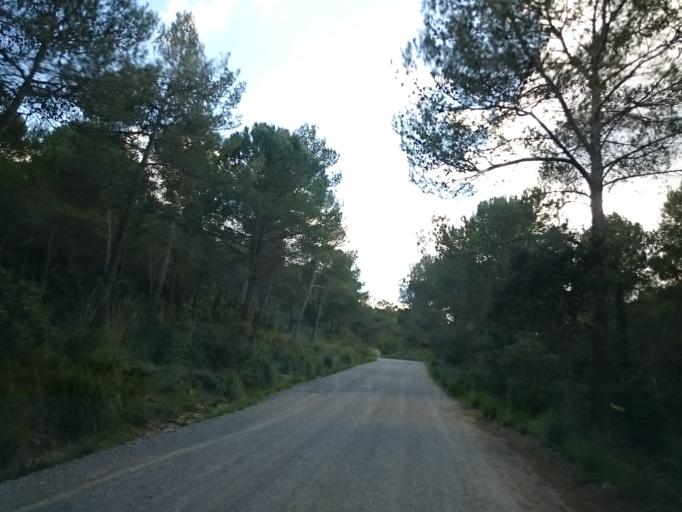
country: ES
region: Catalonia
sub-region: Provincia de Barcelona
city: Begues
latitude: 41.3232
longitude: 1.9226
